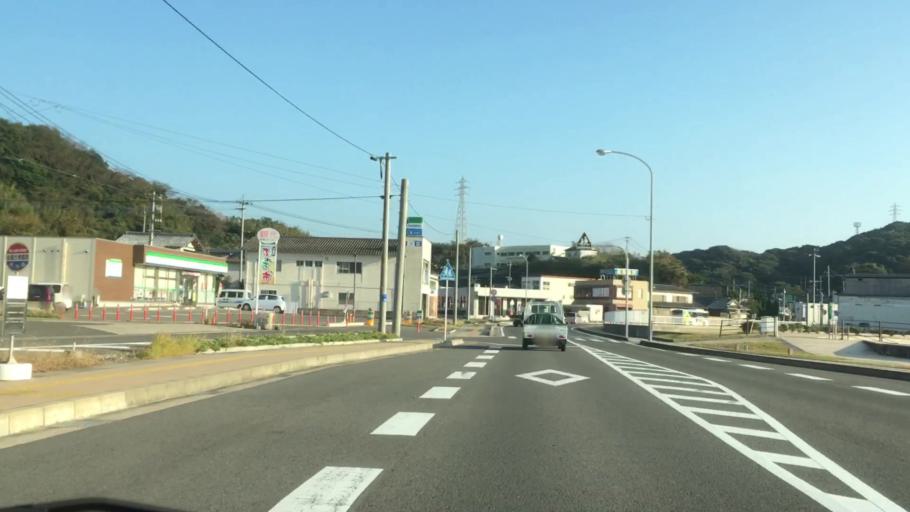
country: JP
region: Nagasaki
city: Togitsu
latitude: 32.9360
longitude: 129.6401
